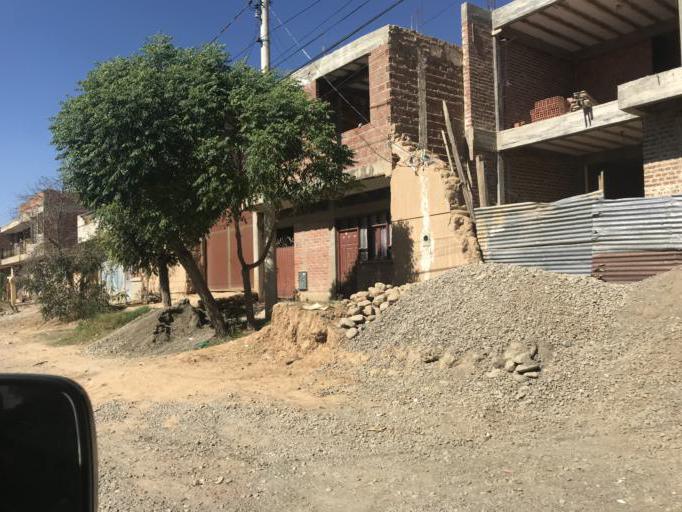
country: BO
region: Cochabamba
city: Cliza
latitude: -17.5815
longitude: -65.9129
